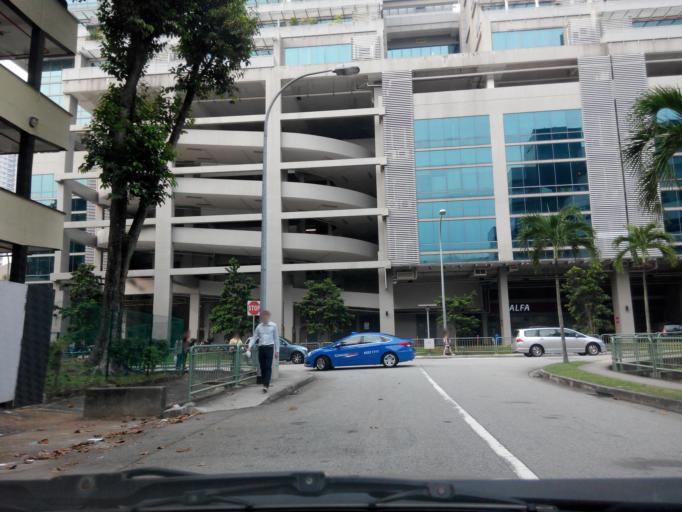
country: SG
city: Singapore
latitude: 1.3047
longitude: 103.7976
